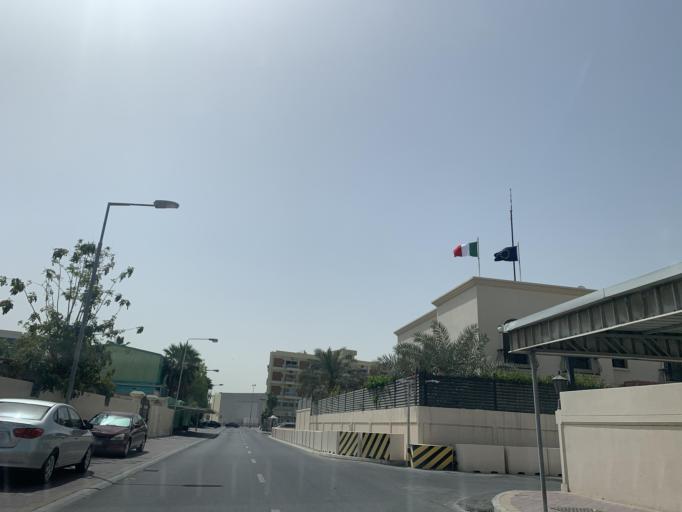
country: BH
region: Manama
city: Jidd Hafs
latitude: 26.2166
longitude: 50.5612
